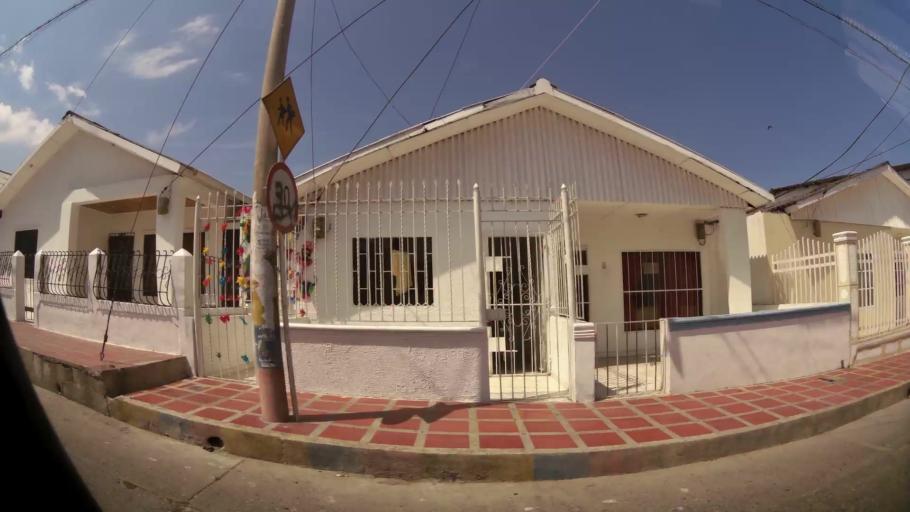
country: CO
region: Atlantico
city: Barranquilla
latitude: 10.9626
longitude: -74.8055
